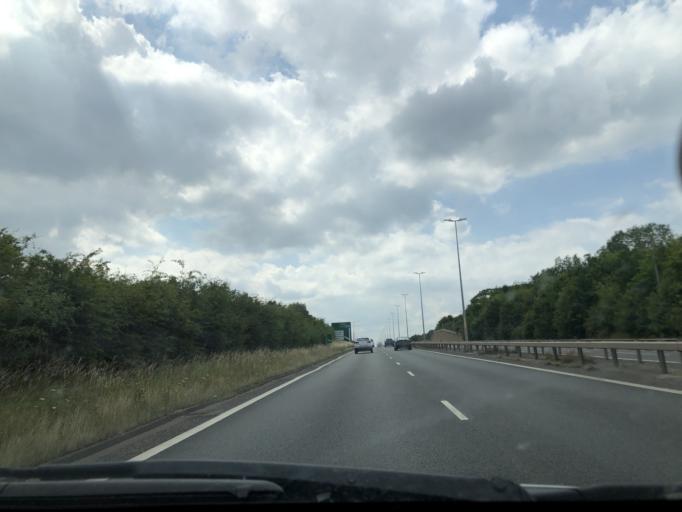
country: GB
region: England
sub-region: Kent
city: Whitstable
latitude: 51.3395
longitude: 1.0318
